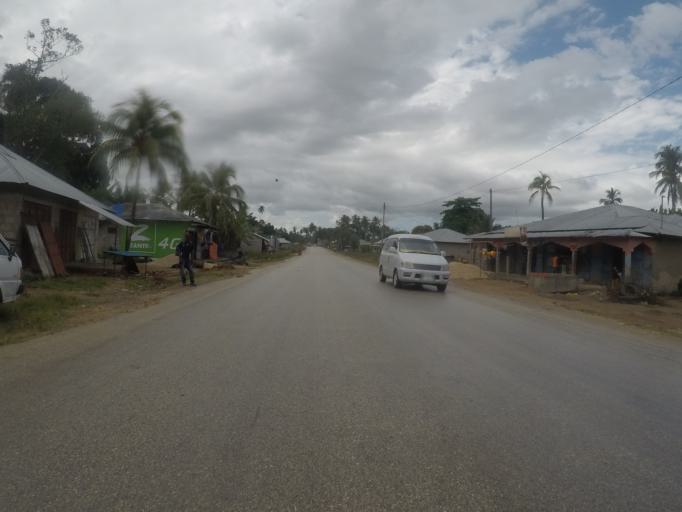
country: TZ
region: Zanzibar Central/South
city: Koani
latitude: -6.0355
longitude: 39.2339
